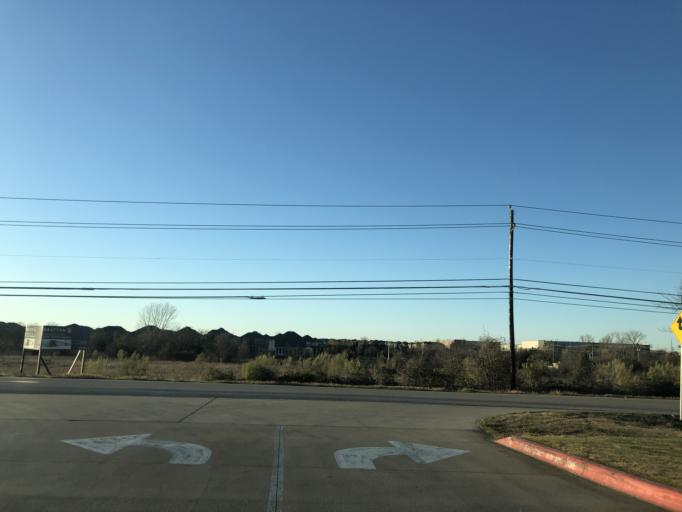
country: US
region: Texas
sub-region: Travis County
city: Wells Branch
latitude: 30.4634
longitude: -97.6736
